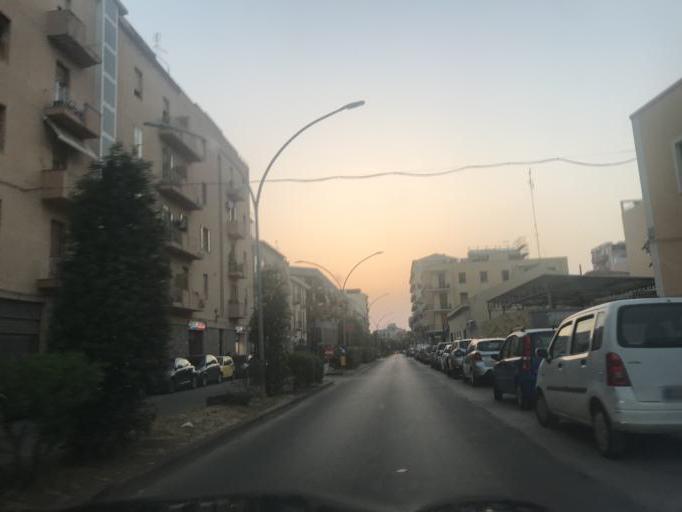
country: IT
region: Sardinia
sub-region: Provincia di Sassari
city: Alghero
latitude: 40.5540
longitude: 8.3222
